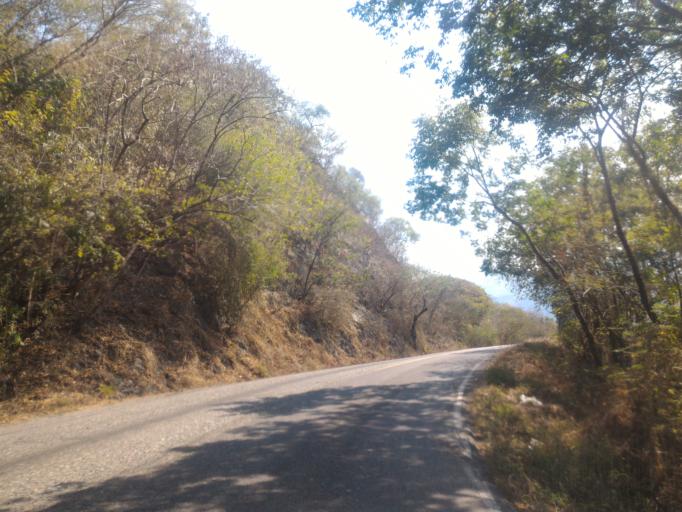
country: MX
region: Michoacan
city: Coahuayana Viejo
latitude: 18.5647
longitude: -103.6388
